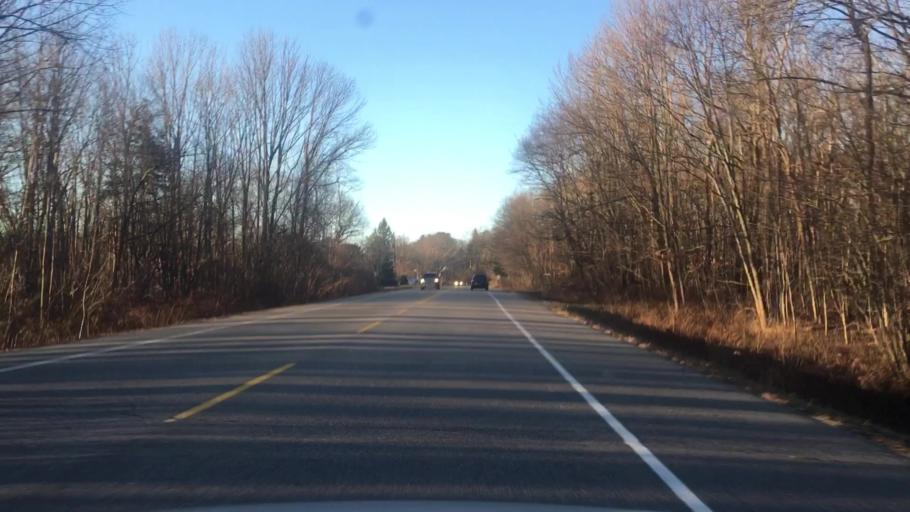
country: US
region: Maine
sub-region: York County
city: South Eliot
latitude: 43.1036
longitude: -70.7607
